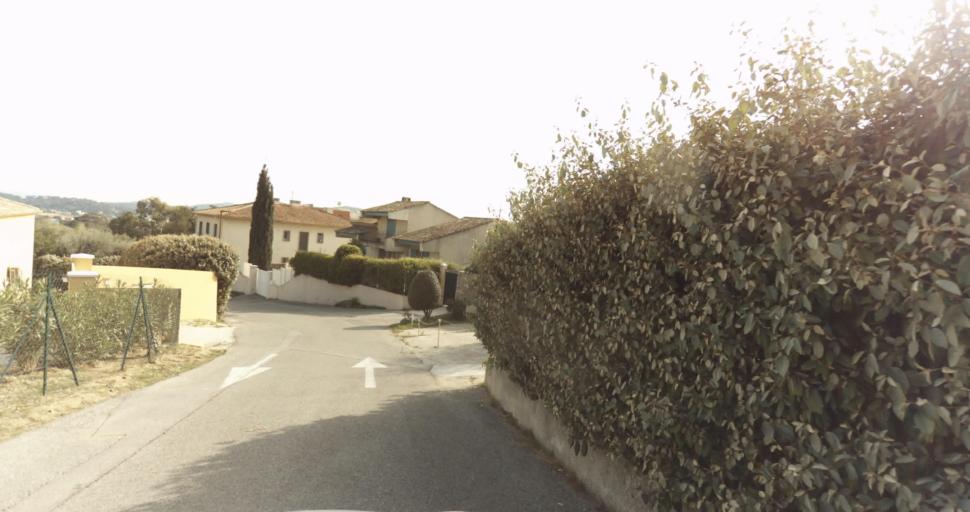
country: FR
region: Provence-Alpes-Cote d'Azur
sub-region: Departement du Var
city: Bormes-les-Mimosas
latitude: 43.1461
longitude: 6.3409
